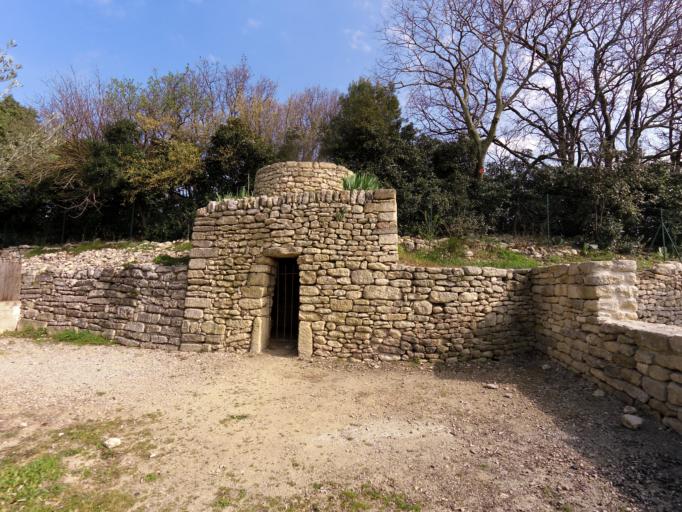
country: FR
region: Languedoc-Roussillon
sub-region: Departement du Gard
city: Villevieille
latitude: 43.7875
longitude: 4.0982
